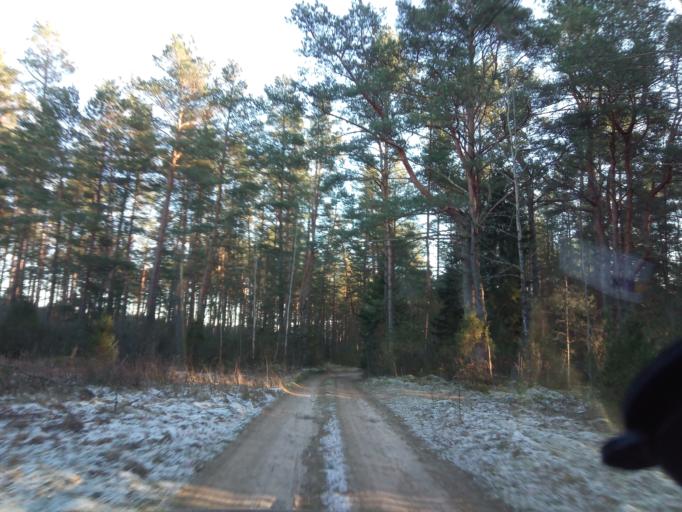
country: LT
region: Alytaus apskritis
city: Druskininkai
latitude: 53.9693
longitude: 23.9677
